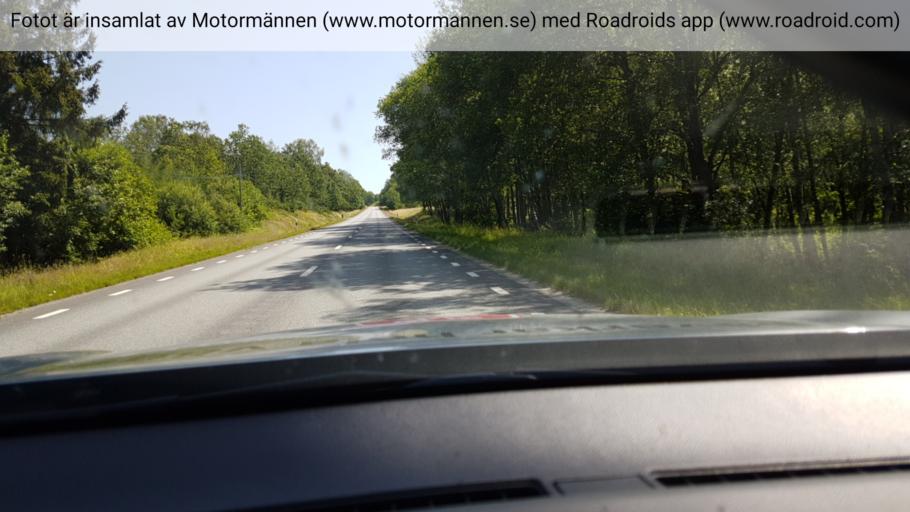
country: SE
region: Joenkoeping
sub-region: Varnamo Kommun
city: Varnamo
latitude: 57.2270
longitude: 14.1344
